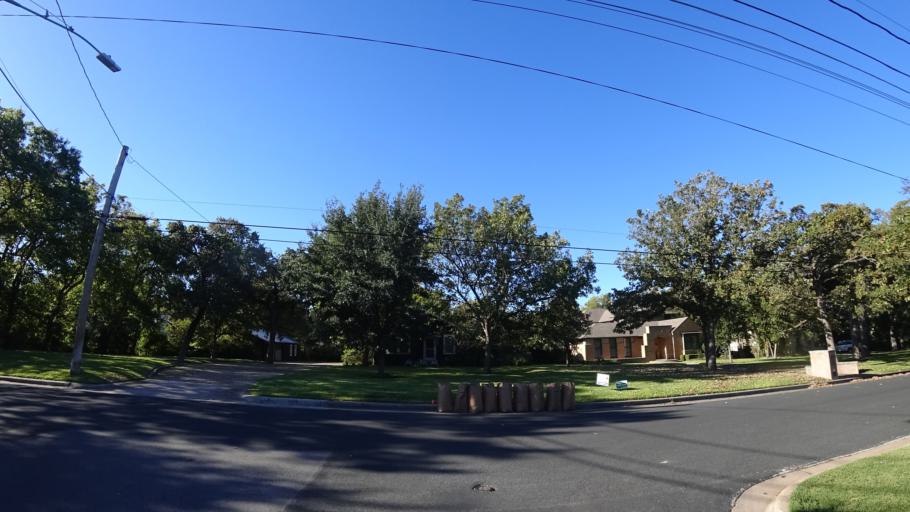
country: US
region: Texas
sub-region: Travis County
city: Rollingwood
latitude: 30.2853
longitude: -97.7676
